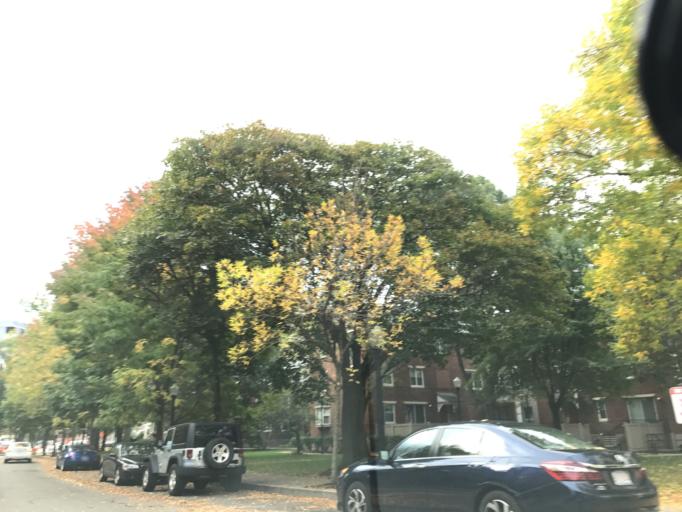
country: US
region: Massachusetts
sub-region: Suffolk County
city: South Boston
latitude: 42.3182
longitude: -71.0401
